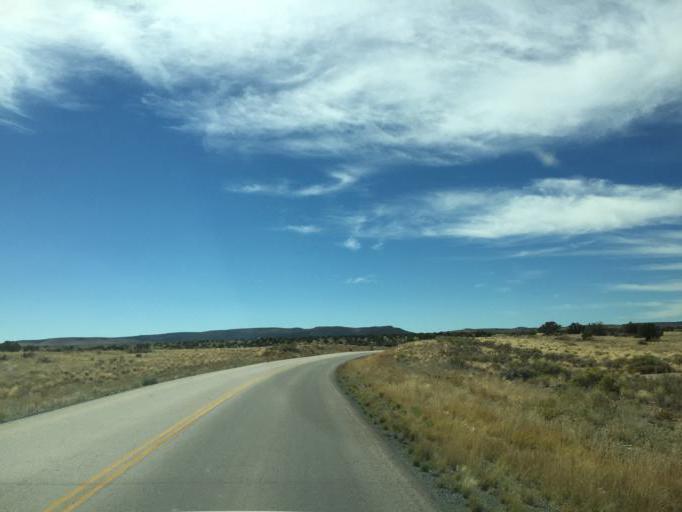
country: US
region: Arizona
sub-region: Mohave County
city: Meadview
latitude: 35.9622
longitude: -113.8268
